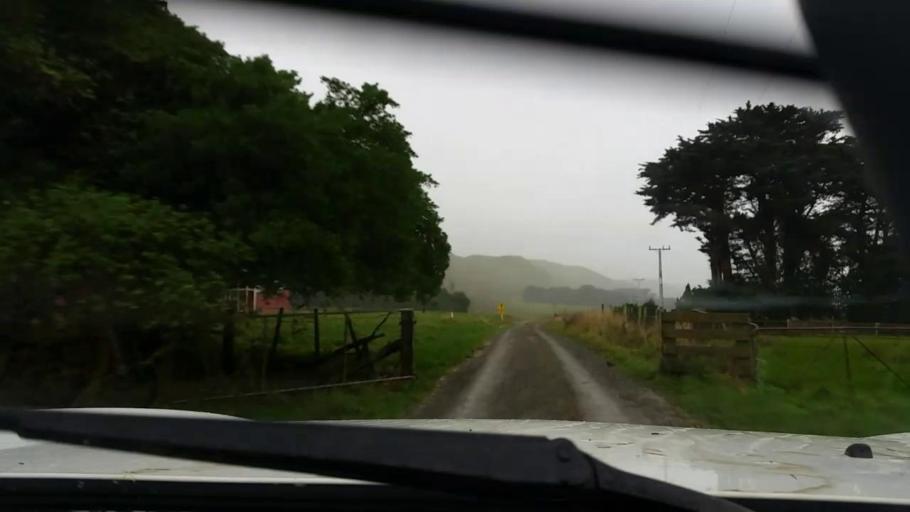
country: NZ
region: Wellington
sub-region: Masterton District
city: Masterton
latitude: -41.2622
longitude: 175.8950
